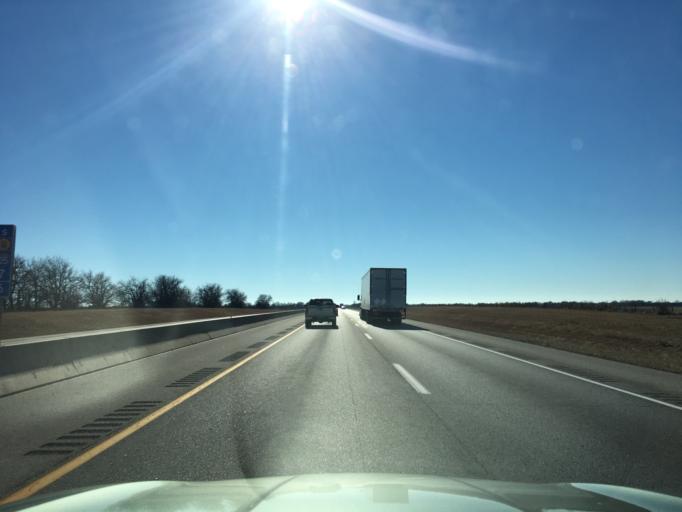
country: US
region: Kansas
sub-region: Sumner County
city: Wellington
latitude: 37.1090
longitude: -97.3388
